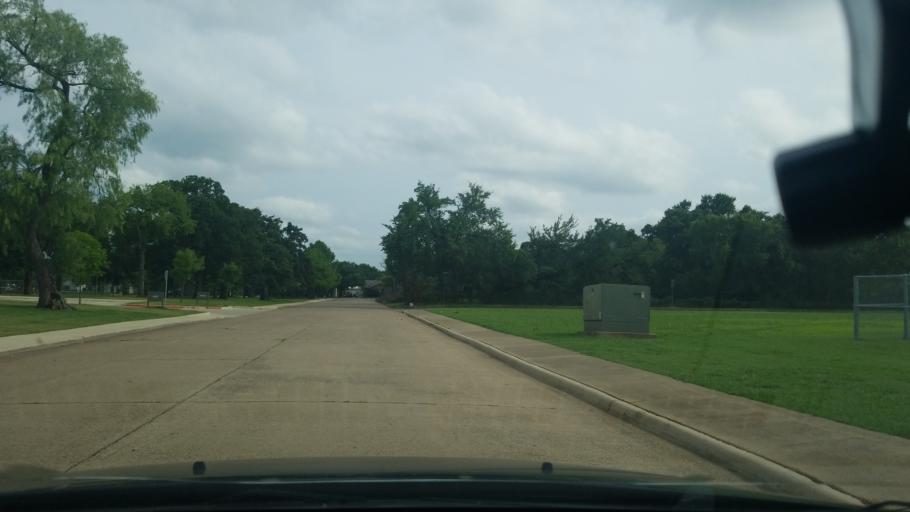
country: US
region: Texas
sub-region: Dallas County
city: Balch Springs
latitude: 32.7595
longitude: -96.6355
